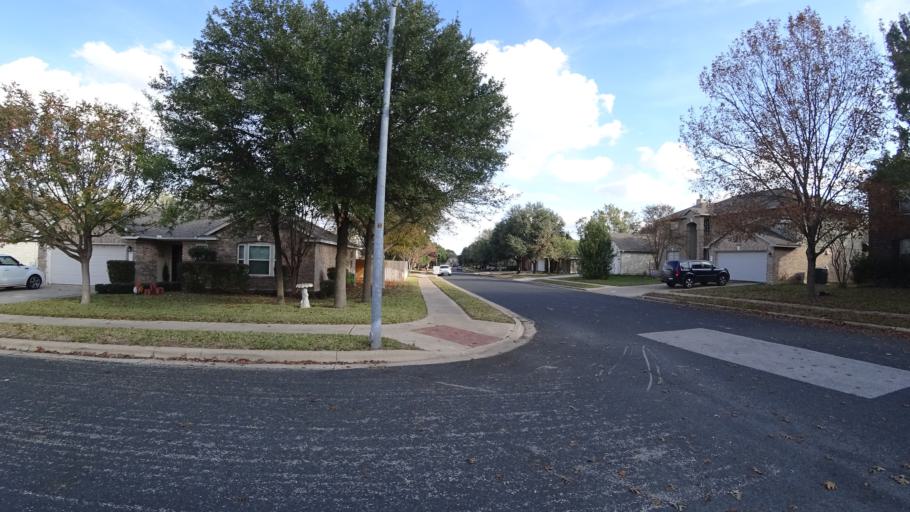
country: US
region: Texas
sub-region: Williamson County
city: Brushy Creek
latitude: 30.5037
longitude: -97.7290
